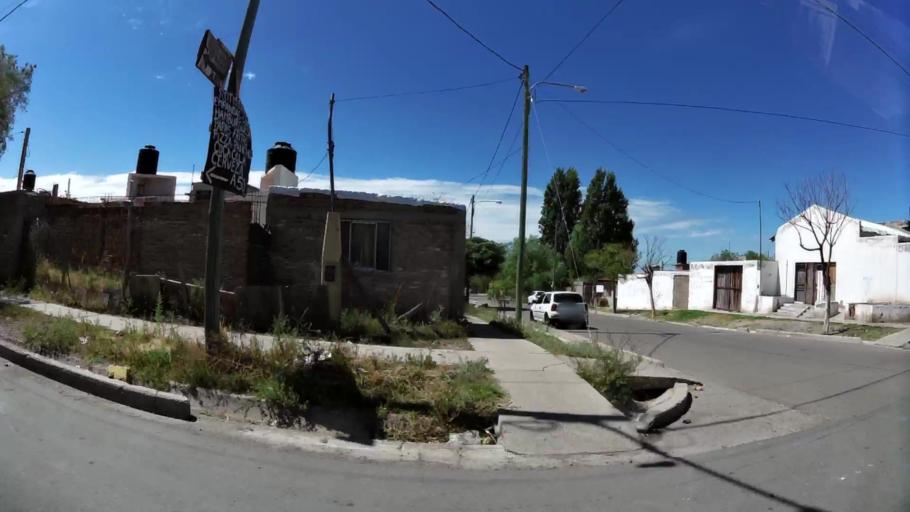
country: AR
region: Mendoza
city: Las Heras
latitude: -32.8516
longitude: -68.8720
